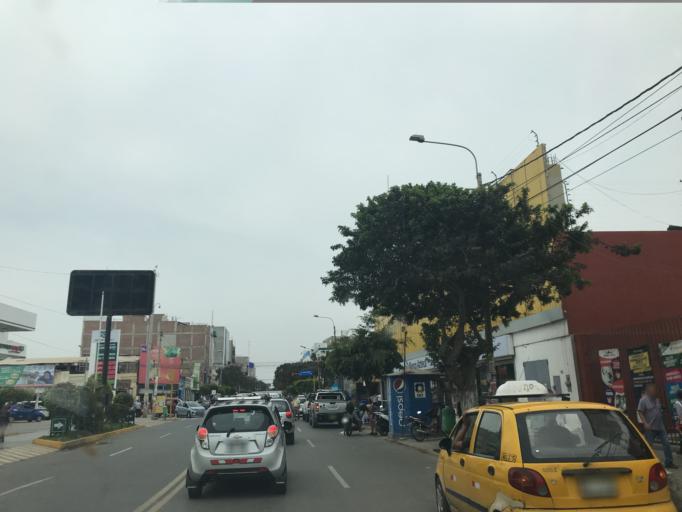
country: PE
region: Lambayeque
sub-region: Provincia de Chiclayo
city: Chiclayo
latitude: -6.7763
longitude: -79.8388
